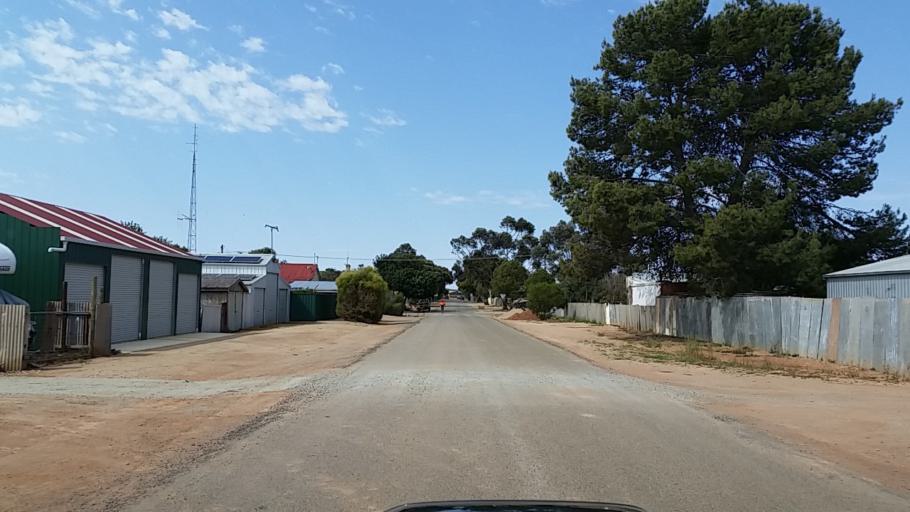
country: AU
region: South Australia
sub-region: Peterborough
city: Peterborough
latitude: -32.9757
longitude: 138.8379
